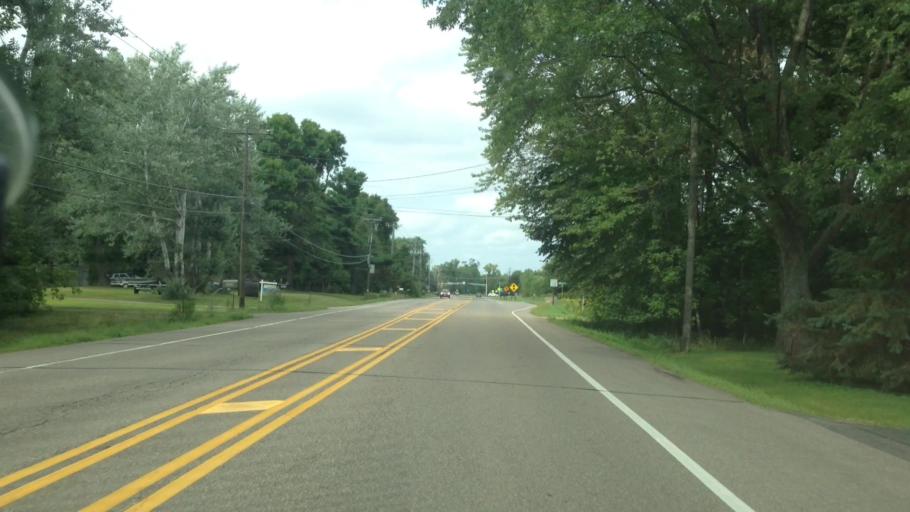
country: US
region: Minnesota
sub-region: Anoka County
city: Circle Pines
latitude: 45.1381
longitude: -93.1270
